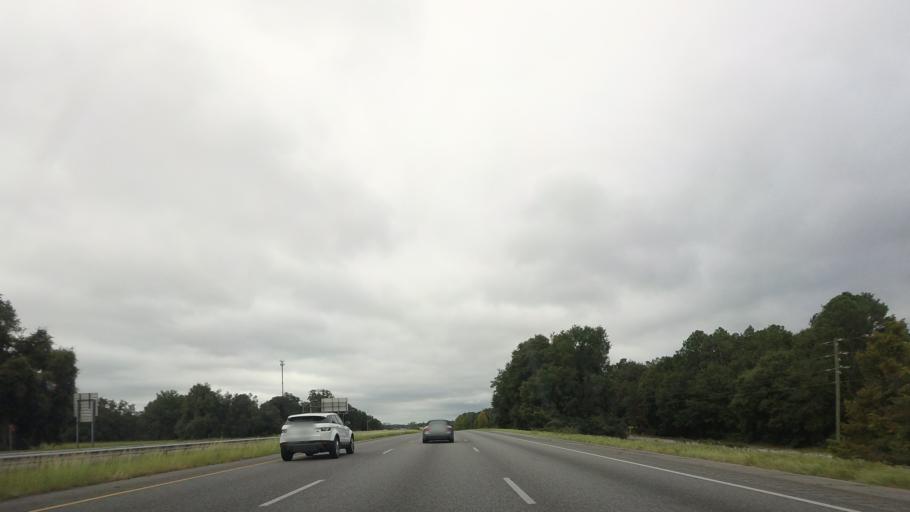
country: US
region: Georgia
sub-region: Echols County
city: Statenville
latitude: 30.6628
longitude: -83.2079
